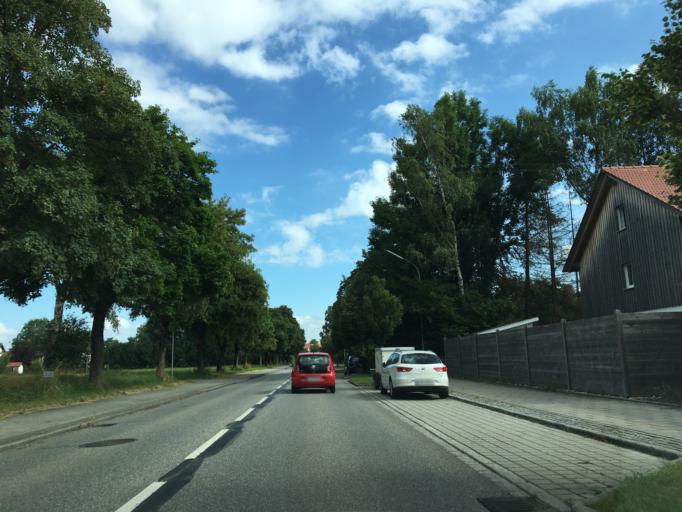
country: DE
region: Bavaria
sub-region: Upper Bavaria
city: Sauerlach
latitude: 47.9671
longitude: 11.6535
